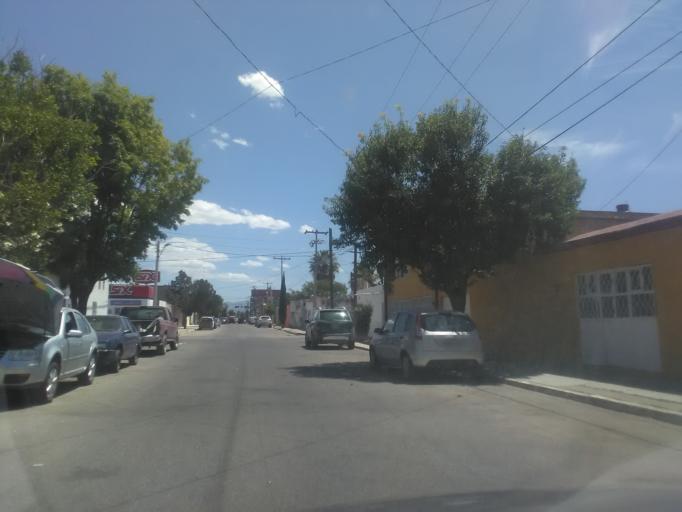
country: MX
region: Durango
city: Victoria de Durango
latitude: 24.0346
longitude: -104.6352
